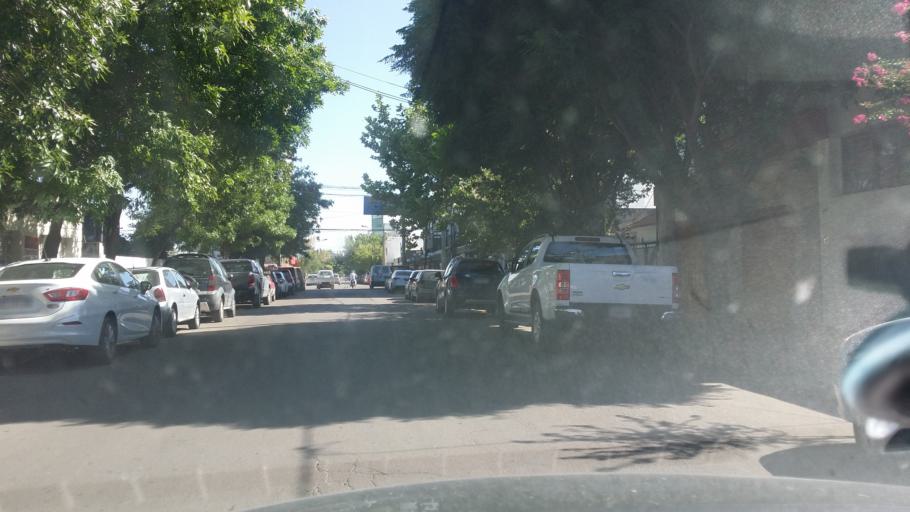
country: AR
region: La Pampa
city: Santa Rosa
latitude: -36.6219
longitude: -64.2821
